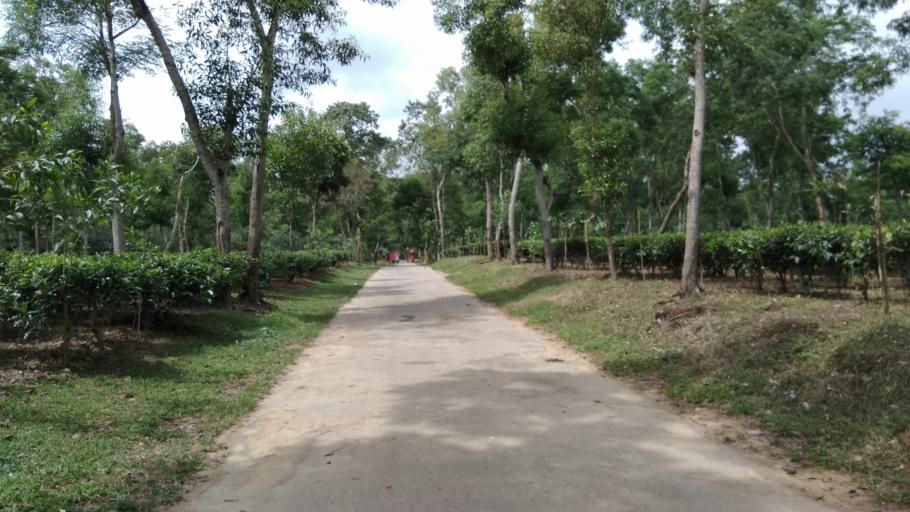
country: IN
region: Tripura
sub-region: Dhalai
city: Kamalpur
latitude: 24.2824
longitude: 91.8251
